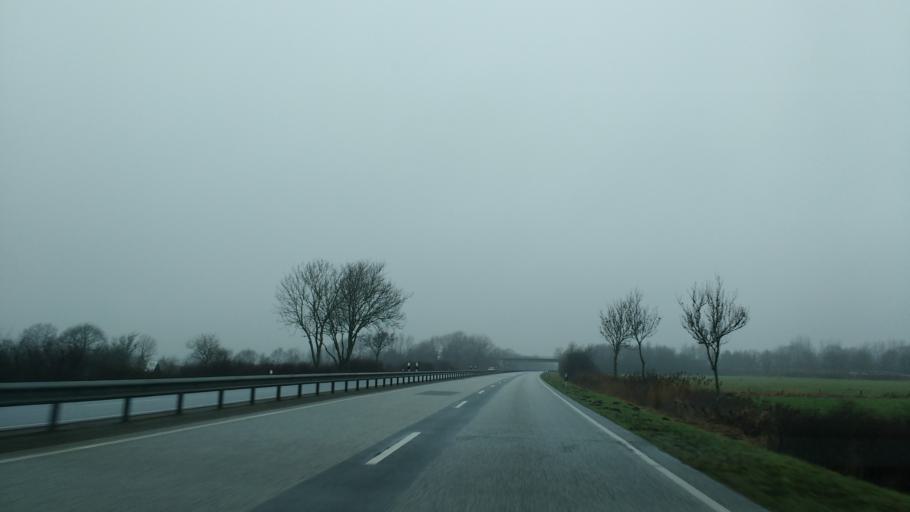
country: DE
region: Schleswig-Holstein
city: Jevenstedt
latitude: 54.2550
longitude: 9.6666
